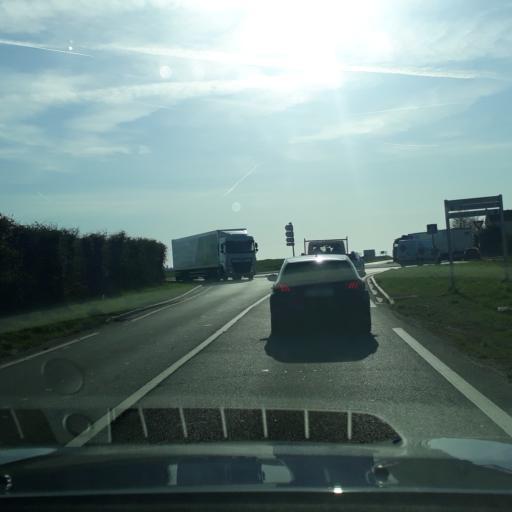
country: FR
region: Ile-de-France
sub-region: Departement de l'Essonne
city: Corbreuse
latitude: 48.4529
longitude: 1.9253
